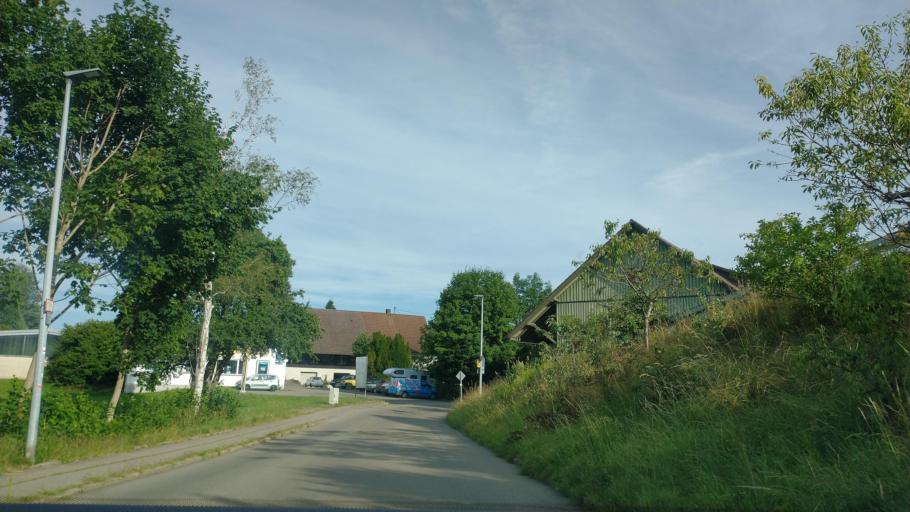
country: DE
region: Baden-Wuerttemberg
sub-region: Tuebingen Region
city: Neukirch
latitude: 47.6598
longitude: 9.7010
